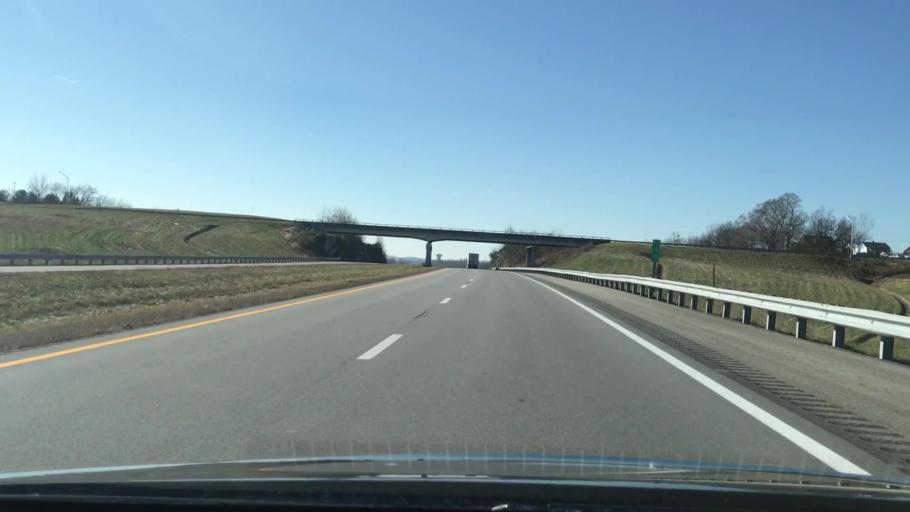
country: US
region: Kentucky
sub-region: Adair County
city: Columbia
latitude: 37.0880
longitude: -85.3008
